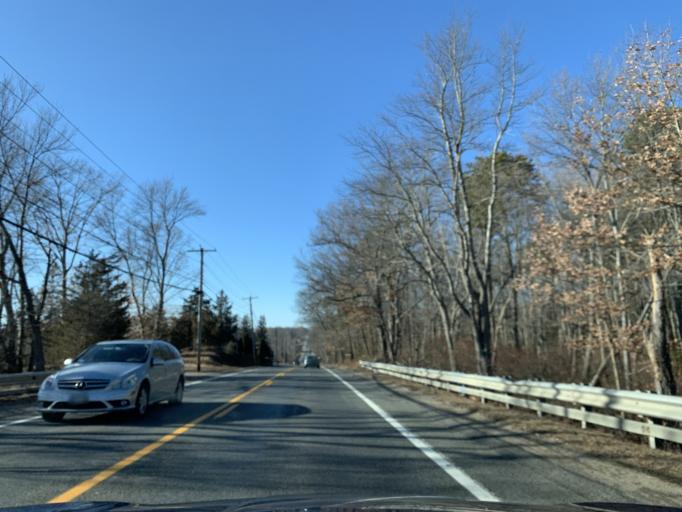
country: US
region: Rhode Island
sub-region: Providence County
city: North Providence
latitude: 41.8964
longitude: -71.4982
